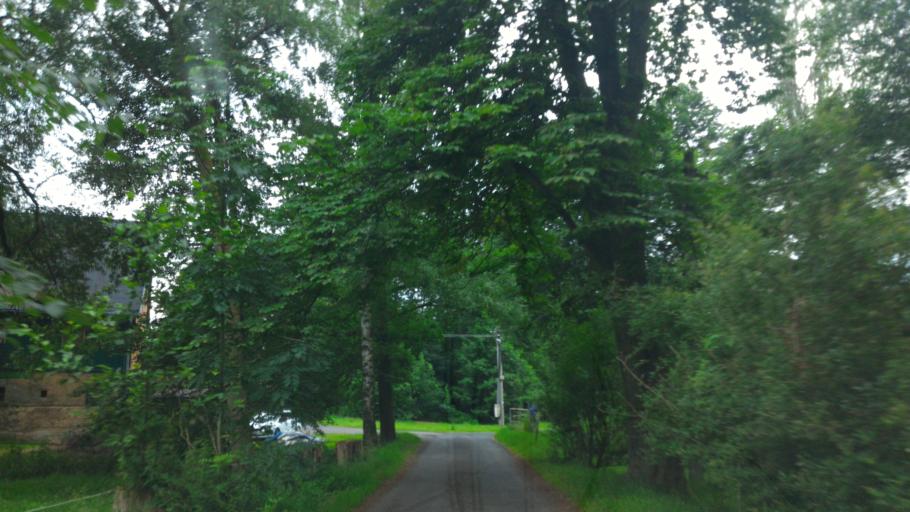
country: CZ
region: Ustecky
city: Varnsdorf
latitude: 50.9140
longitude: 14.6501
